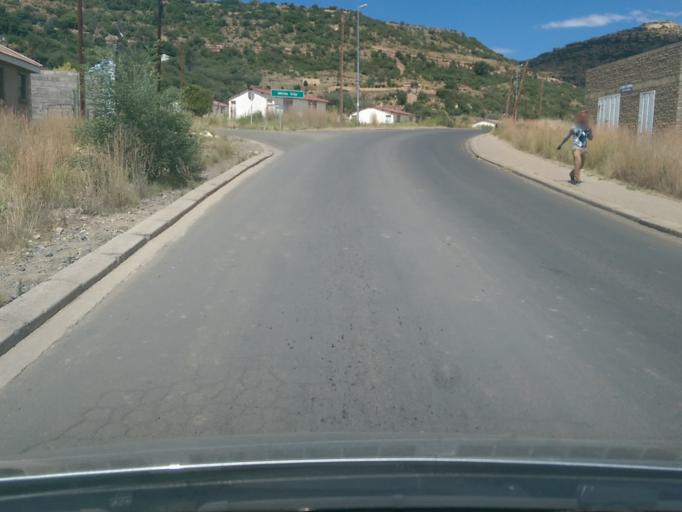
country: LS
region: Maseru
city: Maseru
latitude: -29.3243
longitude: 27.4856
